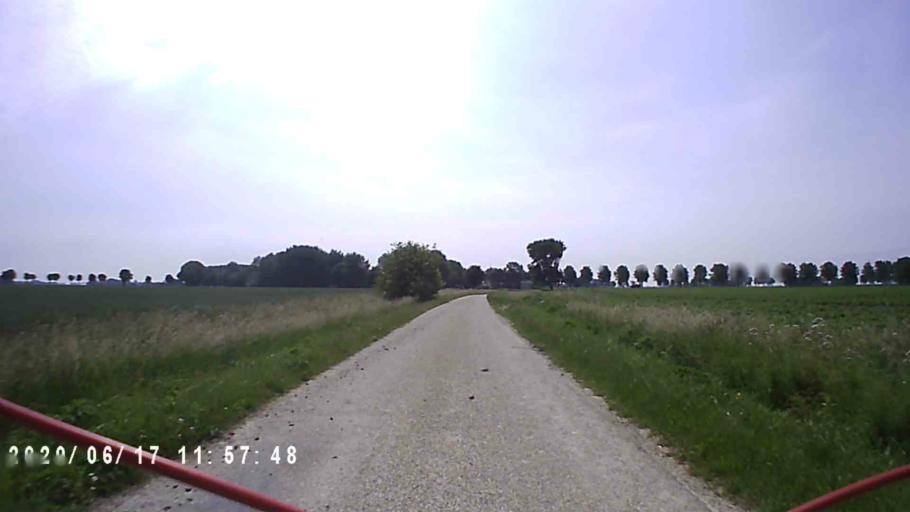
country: NL
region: Groningen
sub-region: Gemeente De Marne
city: Ulrum
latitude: 53.3458
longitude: 6.3260
